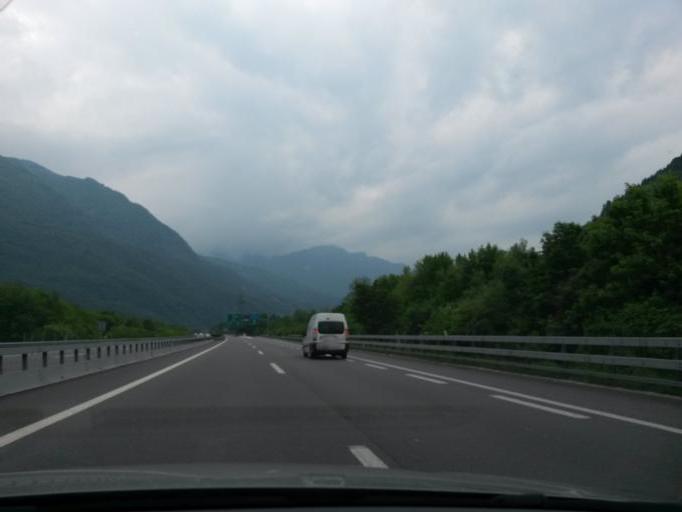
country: CH
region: Ticino
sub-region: Bellinzona District
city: Lumino
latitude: 46.2267
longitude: 9.0341
